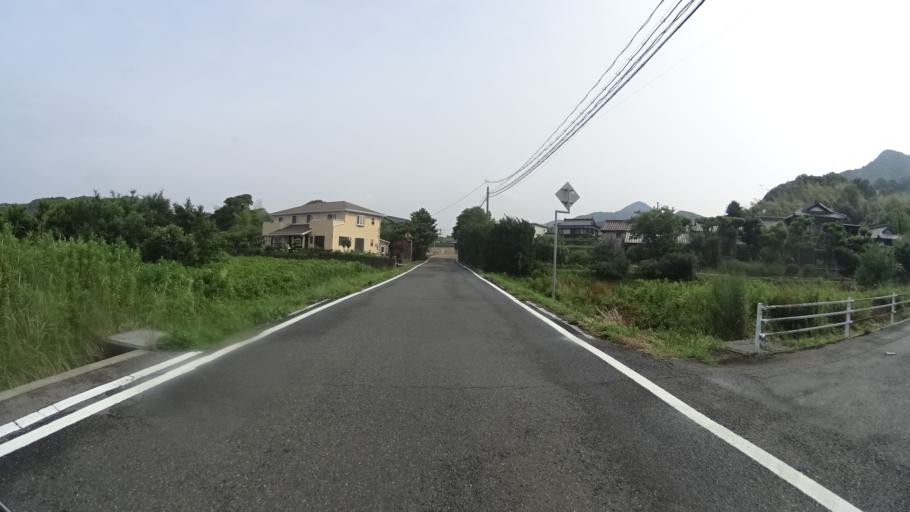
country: JP
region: Yamaguchi
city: Shimonoseki
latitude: 34.0892
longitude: 130.8817
